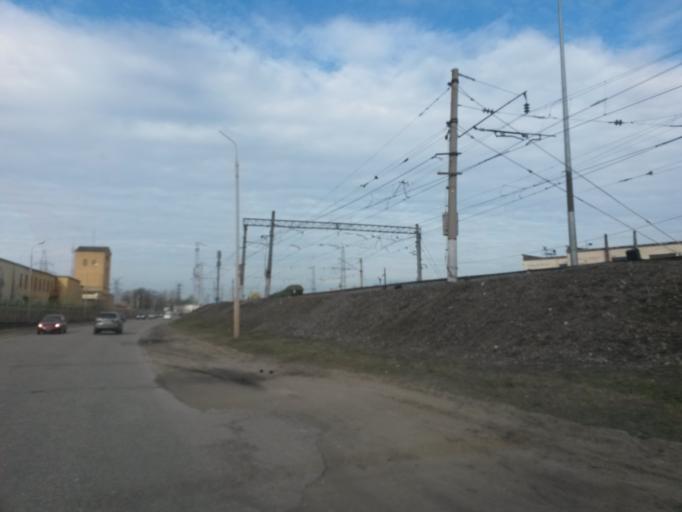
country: RU
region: Jaroslavl
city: Yaroslavl
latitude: 57.6430
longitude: 39.8701
